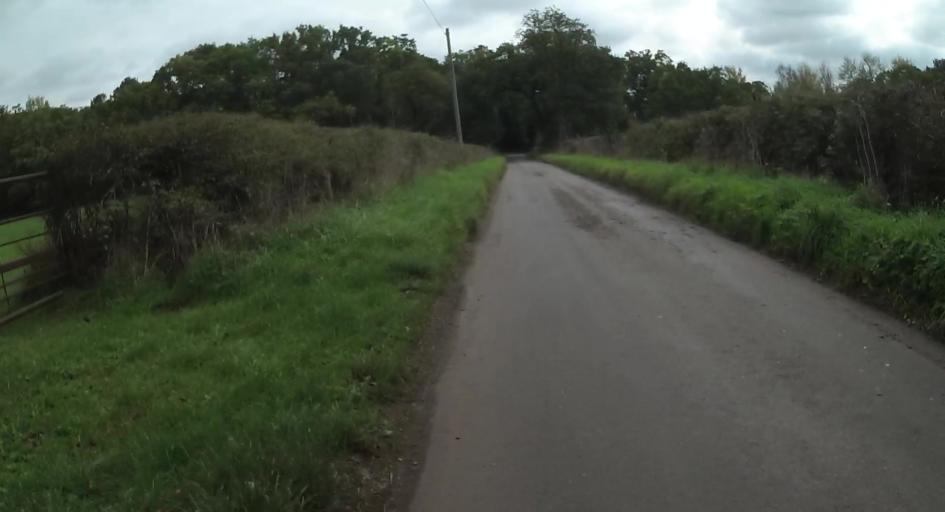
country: GB
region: England
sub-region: Hampshire
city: Eversley
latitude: 51.3622
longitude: -0.9052
